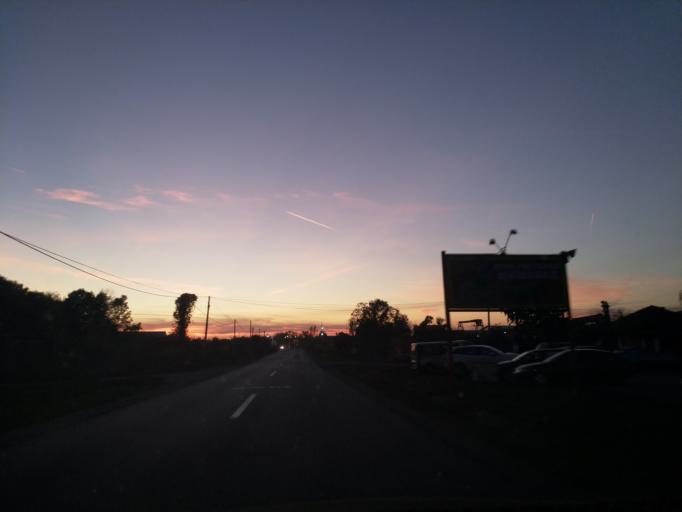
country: RS
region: Central Serbia
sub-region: Sumadijski Okrug
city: Lapovo
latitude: 44.2377
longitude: 21.1278
